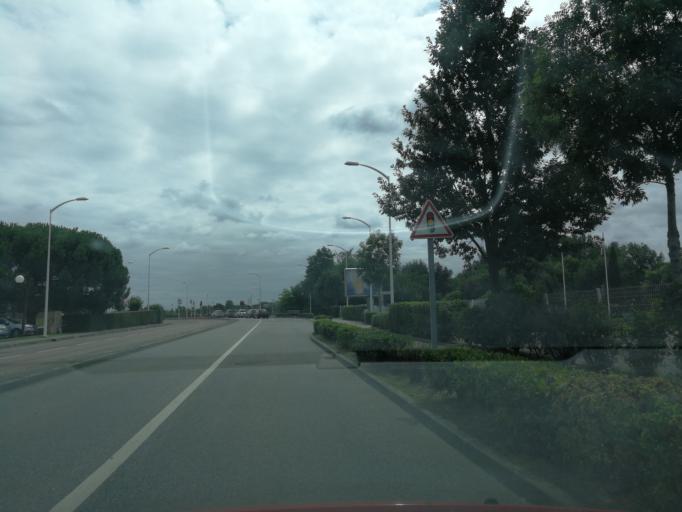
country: FR
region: Midi-Pyrenees
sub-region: Departement de la Haute-Garonne
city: Balma
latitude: 43.5956
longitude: 1.4968
